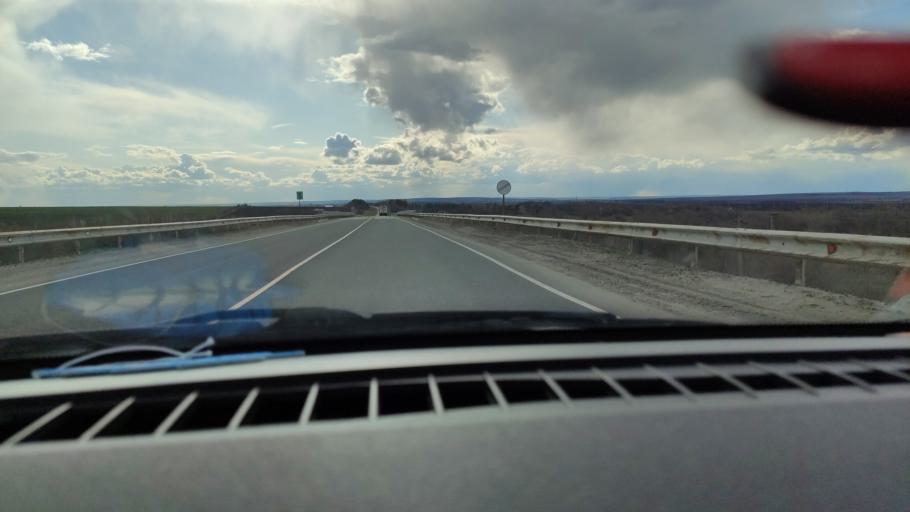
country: RU
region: Saratov
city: Sennoy
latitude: 52.1595
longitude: 47.0381
